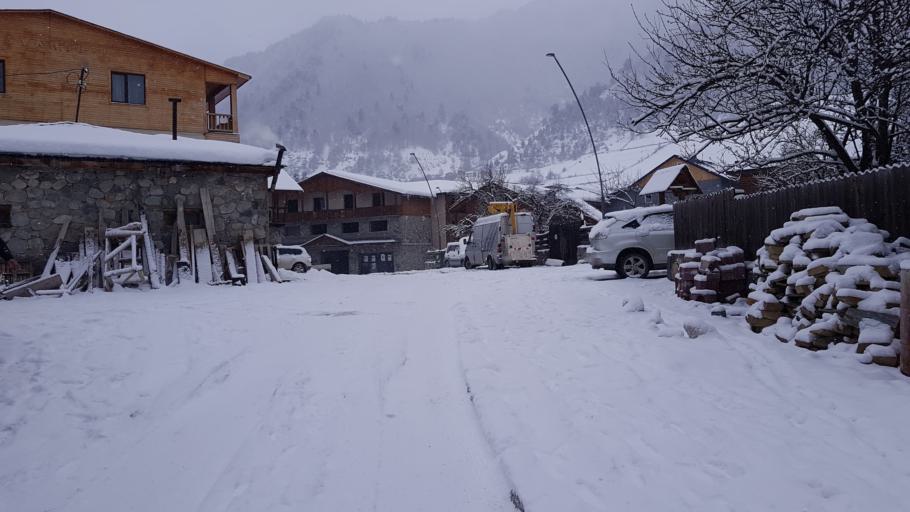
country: GE
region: Samegrelo and Zemo Svaneti
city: Mest'ia
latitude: 43.0433
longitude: 42.7265
